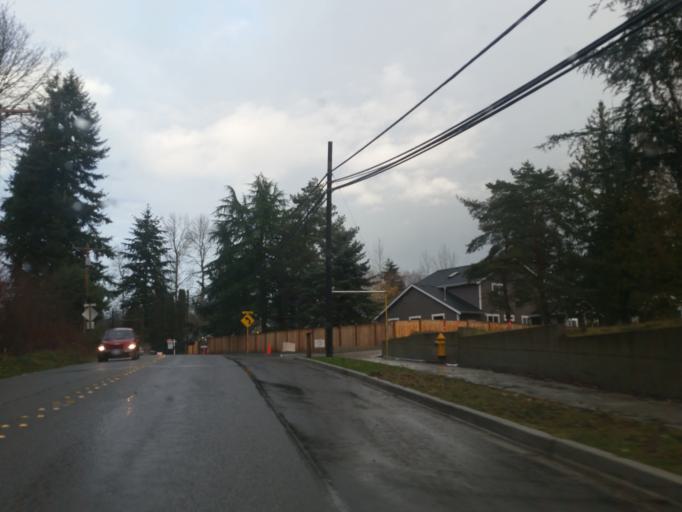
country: US
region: Washington
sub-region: Snohomish County
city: Brier
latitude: 47.7896
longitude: -122.2558
